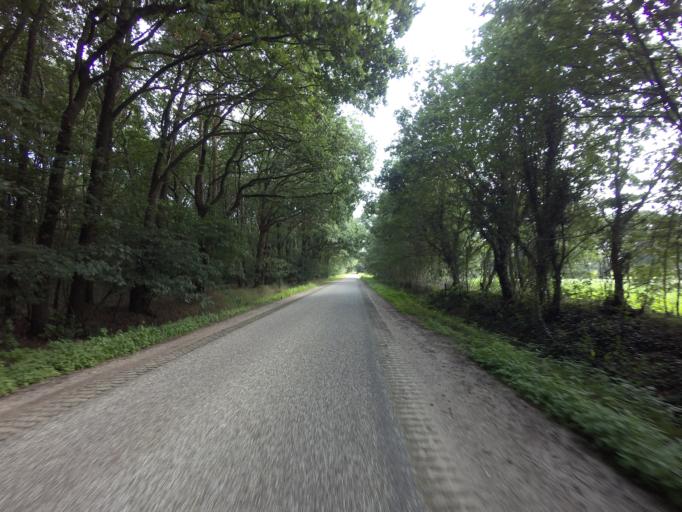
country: DE
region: Lower Saxony
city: Getelo
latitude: 52.4117
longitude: 6.8442
